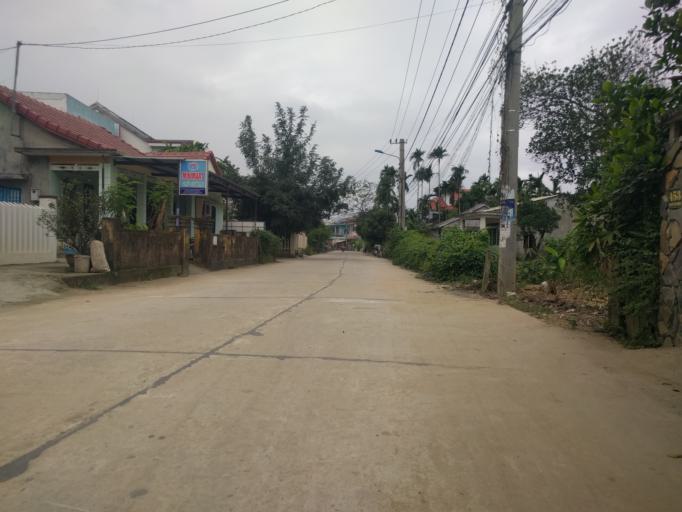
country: VN
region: Quang Nam
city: Hoi An
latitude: 15.8696
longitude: 108.3500
